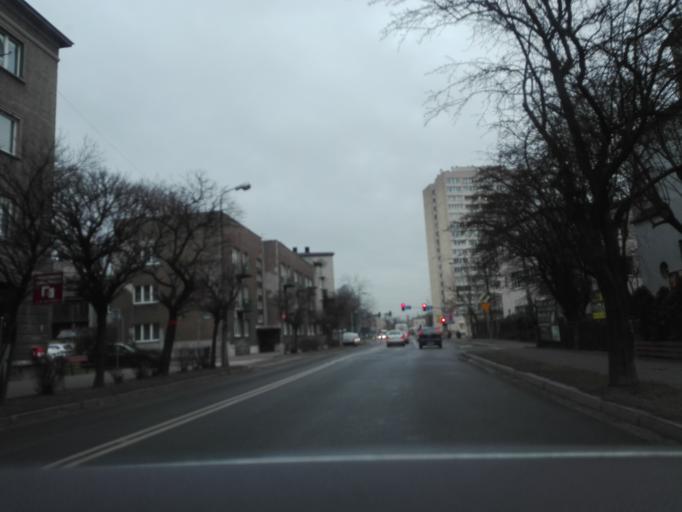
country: PL
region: Silesian Voivodeship
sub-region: Katowice
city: Katowice
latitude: 50.2707
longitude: 19.0228
